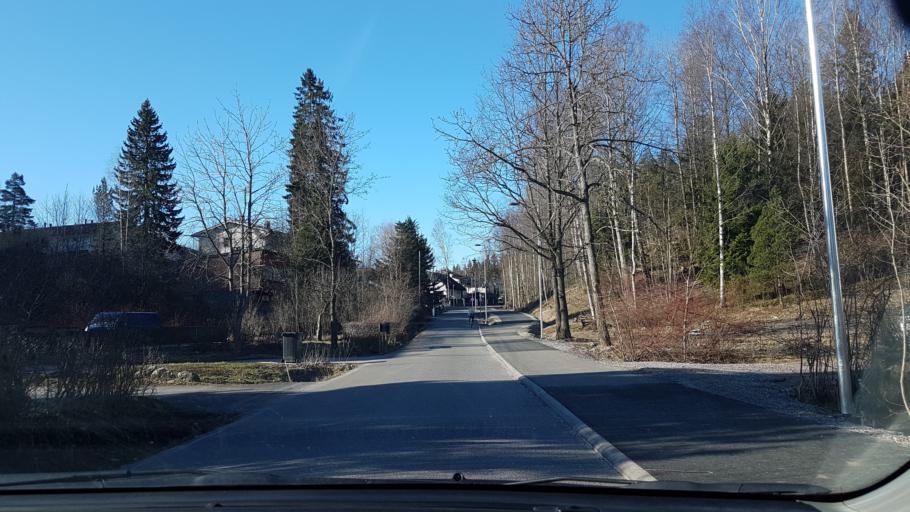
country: FI
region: Uusimaa
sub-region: Helsinki
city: Vantaa
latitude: 60.2710
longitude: 25.0910
